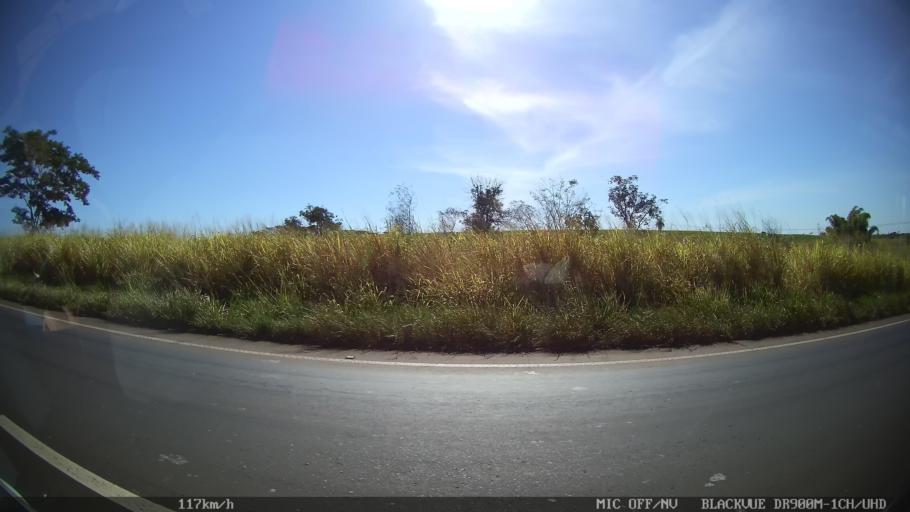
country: BR
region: Sao Paulo
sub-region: Olimpia
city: Olimpia
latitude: -20.6344
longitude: -48.8170
